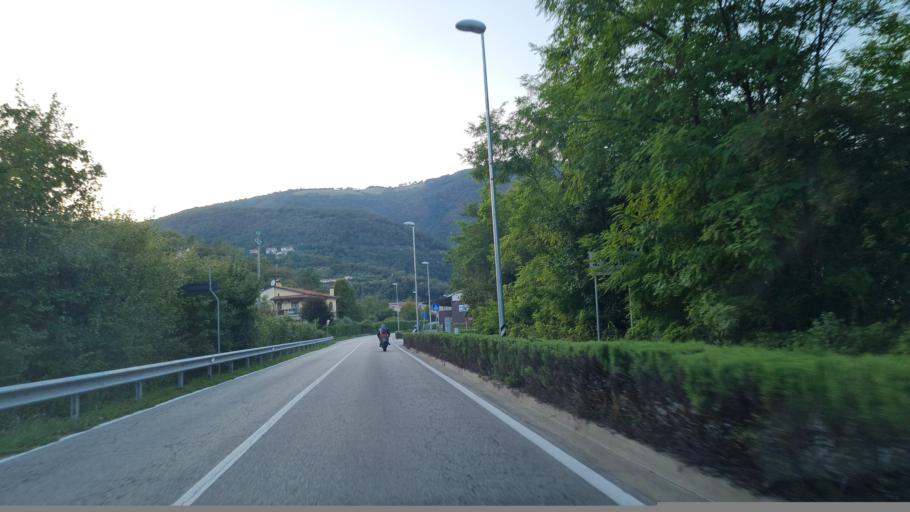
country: IT
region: Veneto
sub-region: Provincia di Vicenza
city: Campese
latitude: 45.7723
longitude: 11.6939
